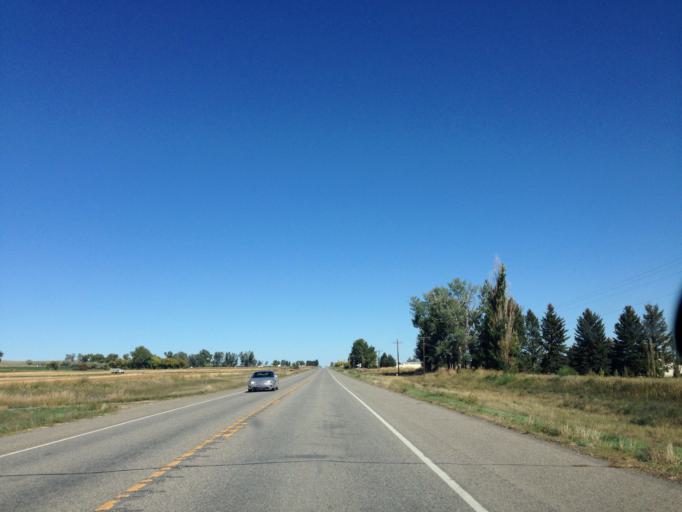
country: US
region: Montana
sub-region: Yellowstone County
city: Laurel
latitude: 45.4688
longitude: -108.8630
